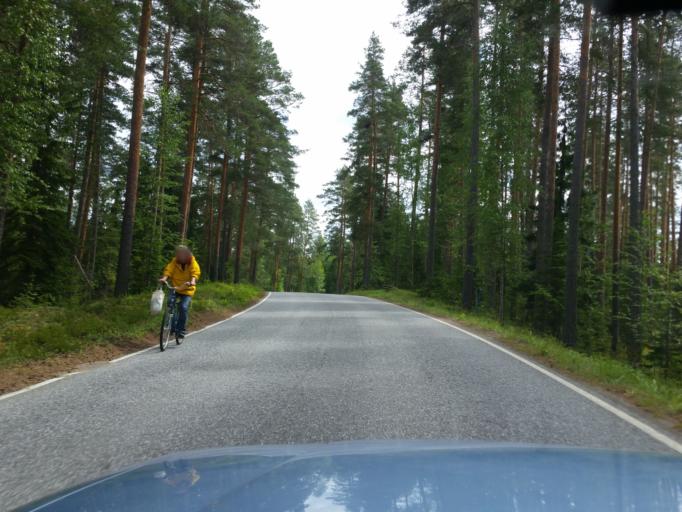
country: FI
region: Southern Savonia
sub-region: Savonlinna
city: Sulkava
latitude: 61.7932
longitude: 28.4199
